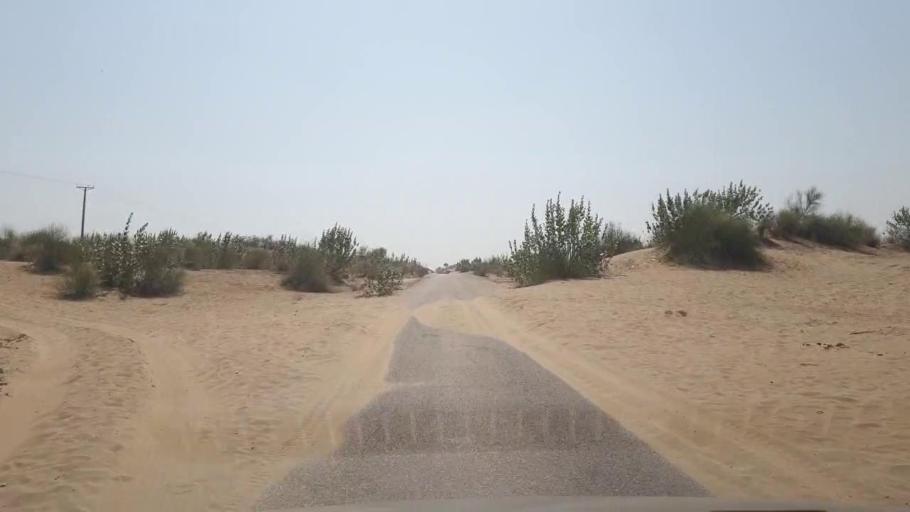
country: PK
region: Sindh
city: Chor
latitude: 25.6388
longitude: 70.1726
